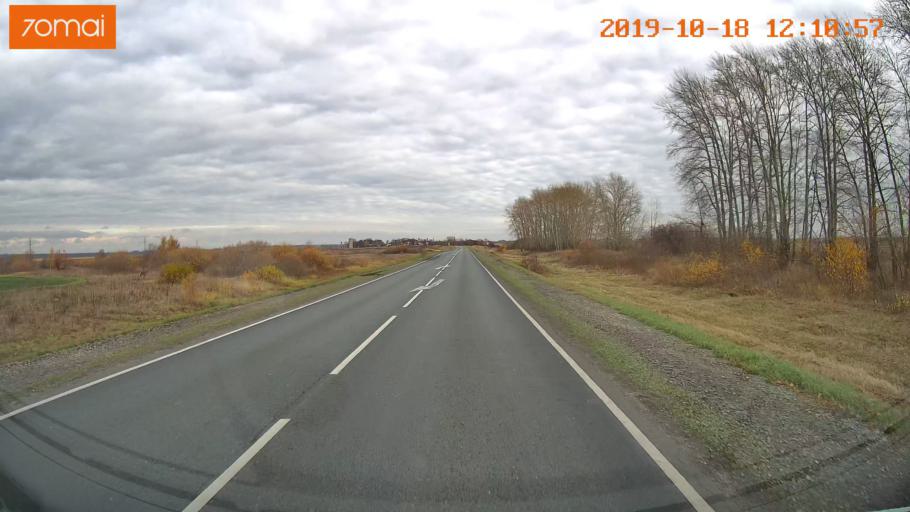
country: RU
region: Rjazan
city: Zakharovo
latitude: 54.3968
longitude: 39.3422
